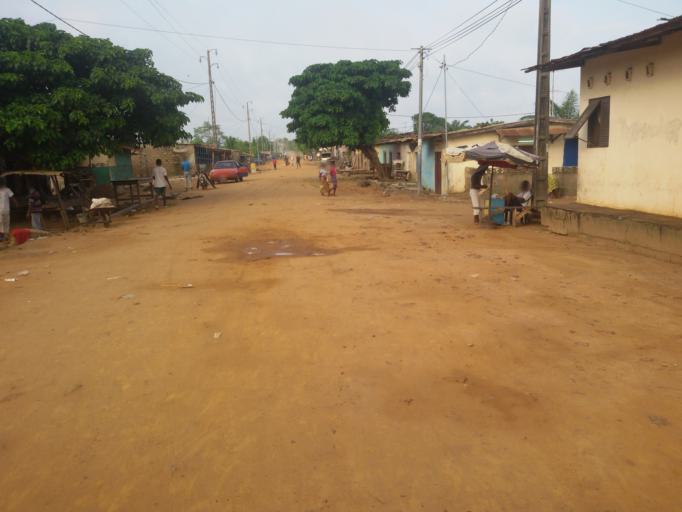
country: CI
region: Sud-Comoe
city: Grand-Bassam
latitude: 5.2047
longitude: -3.7323
